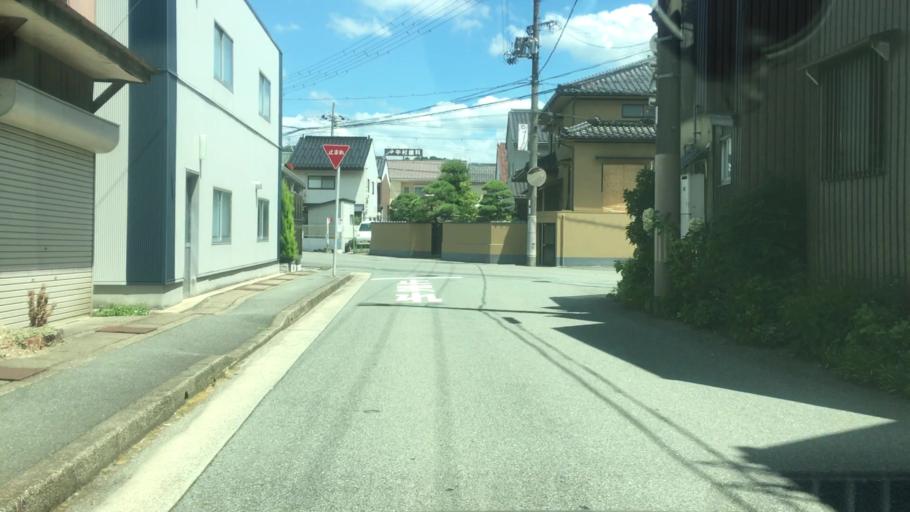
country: JP
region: Hyogo
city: Toyooka
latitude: 35.5490
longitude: 134.8234
